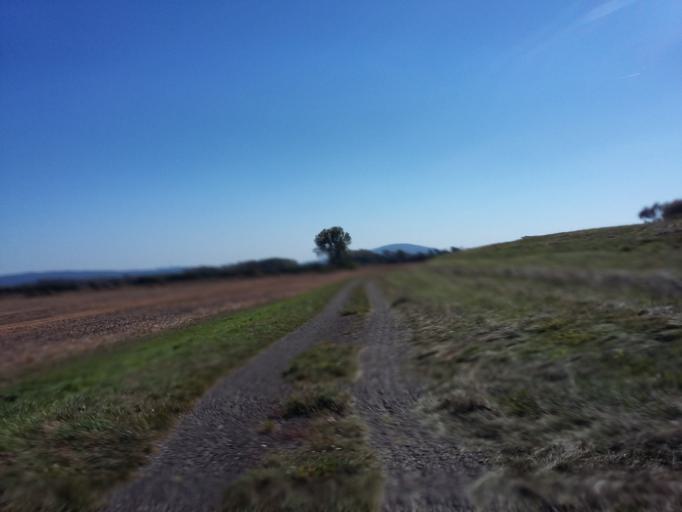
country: AT
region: Lower Austria
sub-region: Politischer Bezirk Ganserndorf
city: Marchegg
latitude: 48.3079
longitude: 16.9247
